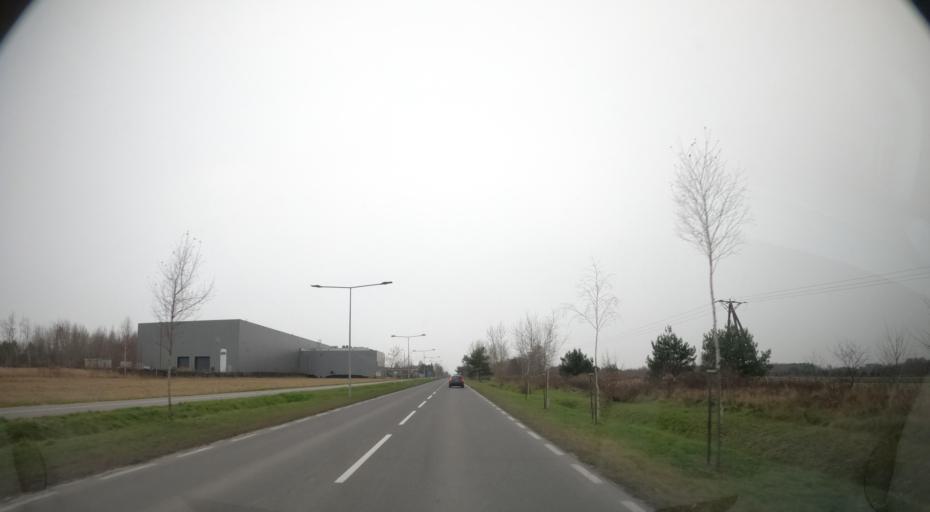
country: PL
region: Masovian Voivodeship
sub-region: Radom
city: Radom
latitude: 51.4484
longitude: 21.1929
